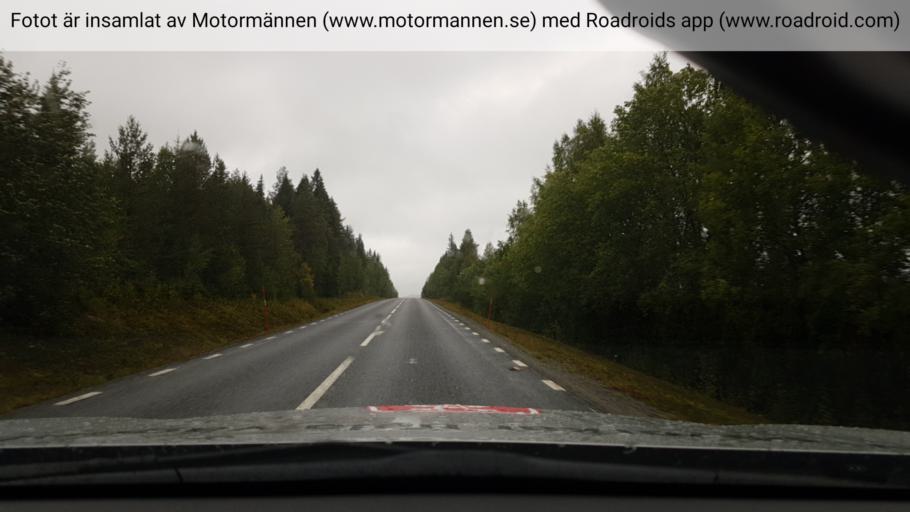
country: SE
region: Vaesterbotten
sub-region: Lycksele Kommun
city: Lycksele
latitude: 64.0468
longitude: 18.5702
